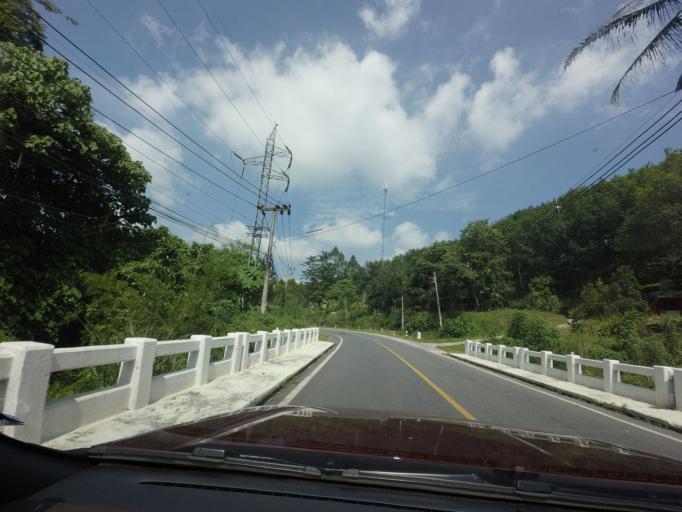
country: TH
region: Yala
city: Betong
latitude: 5.8319
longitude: 101.1135
